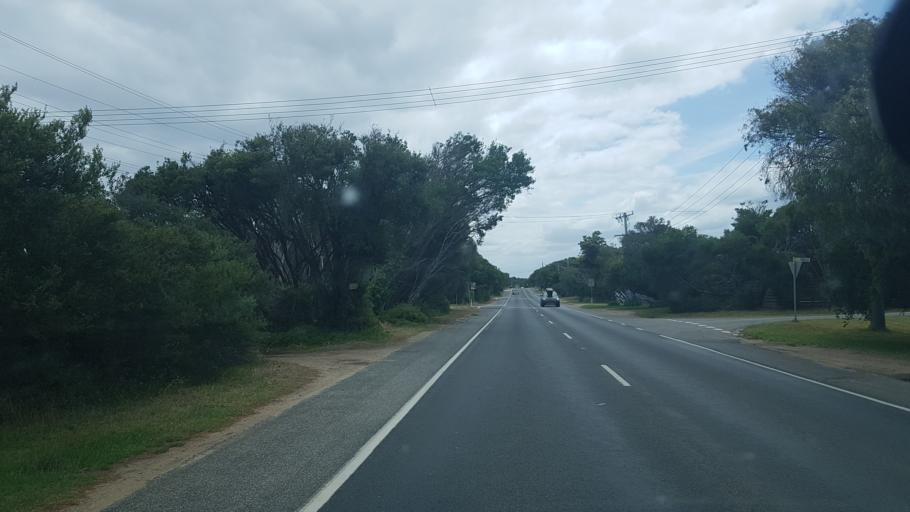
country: AU
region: Victoria
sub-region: Mornington Peninsula
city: Blairgowrie
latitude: -38.3741
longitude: 144.7777
